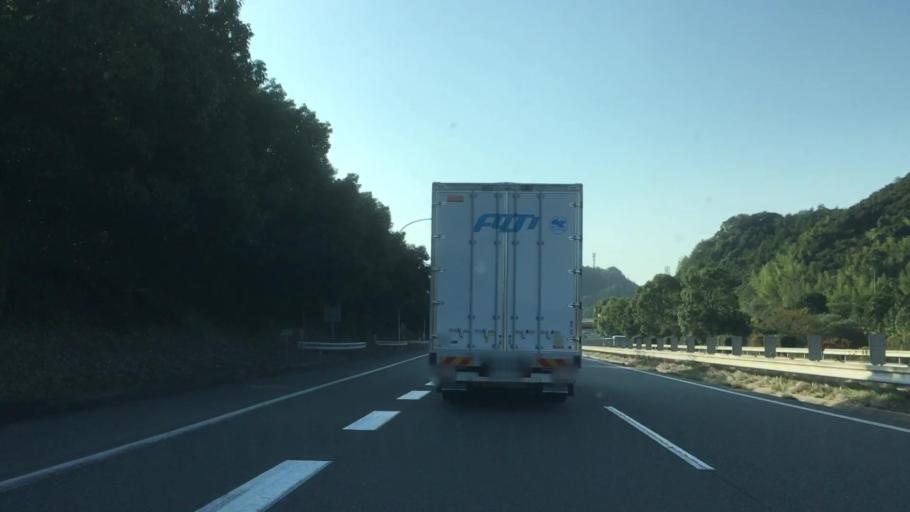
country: JP
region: Yamaguchi
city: Ogori-shimogo
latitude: 34.0858
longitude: 131.4686
